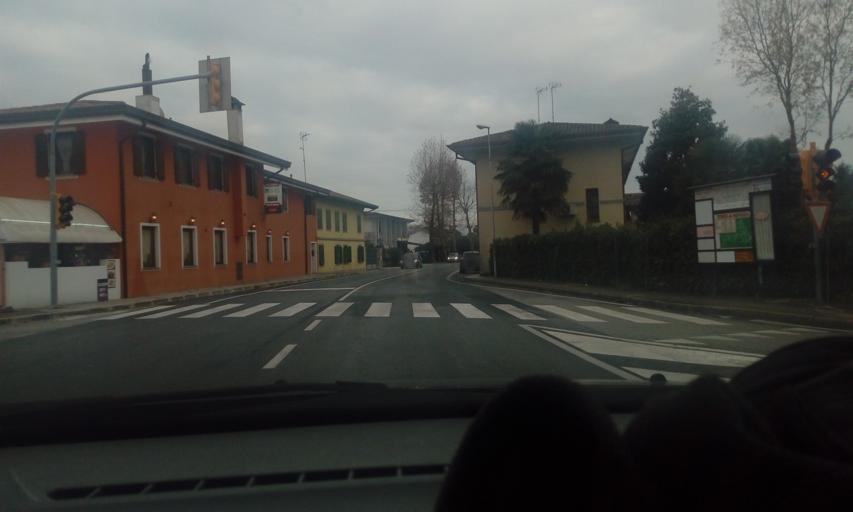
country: IT
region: Friuli Venezia Giulia
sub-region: Provincia di Udine
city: Terzo d'Aquileia
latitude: 45.7989
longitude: 13.3513
